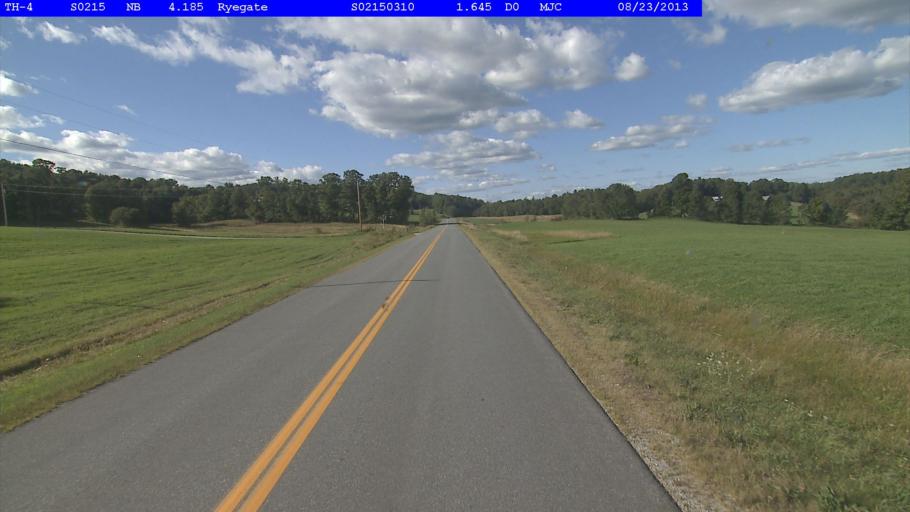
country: US
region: New Hampshire
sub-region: Grafton County
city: Woodsville
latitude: 44.2647
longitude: -72.1721
